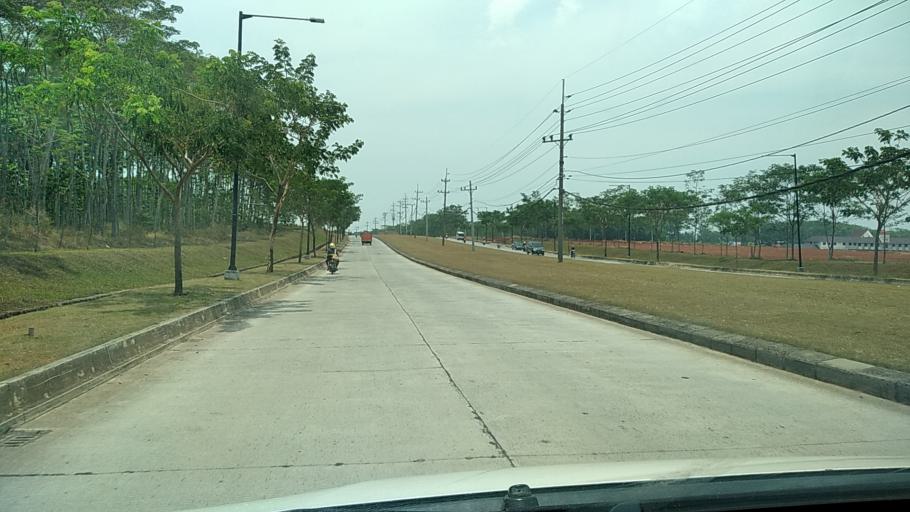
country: ID
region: Central Java
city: Semarang
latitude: -7.0382
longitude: 110.3313
